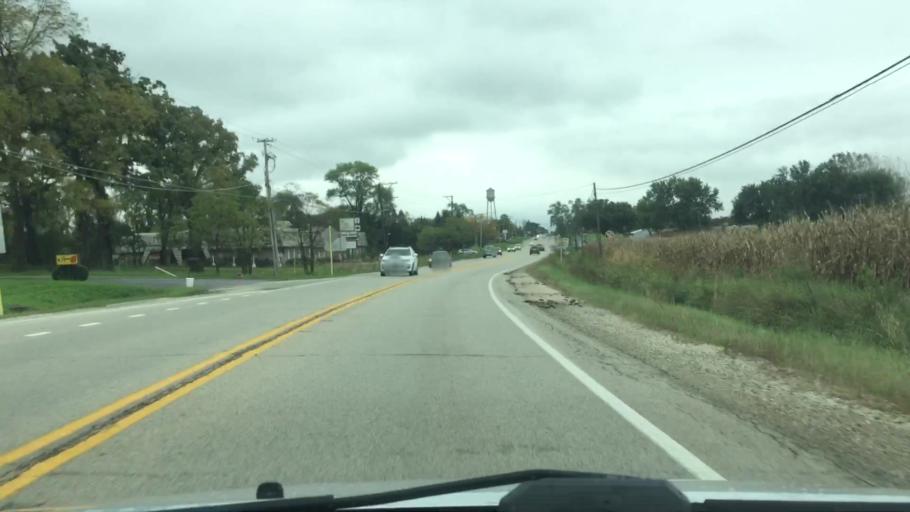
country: US
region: Illinois
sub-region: McHenry County
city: Richmond
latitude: 42.4887
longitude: -88.3062
